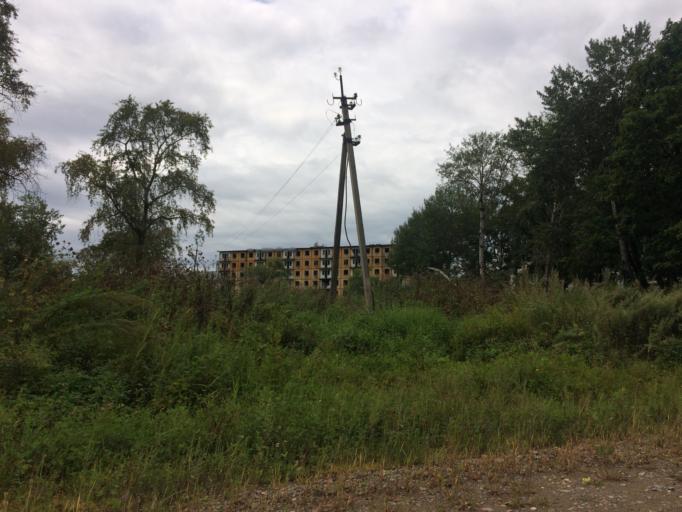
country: RU
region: Primorskiy
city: Lazo
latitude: 45.8225
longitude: 133.6440
